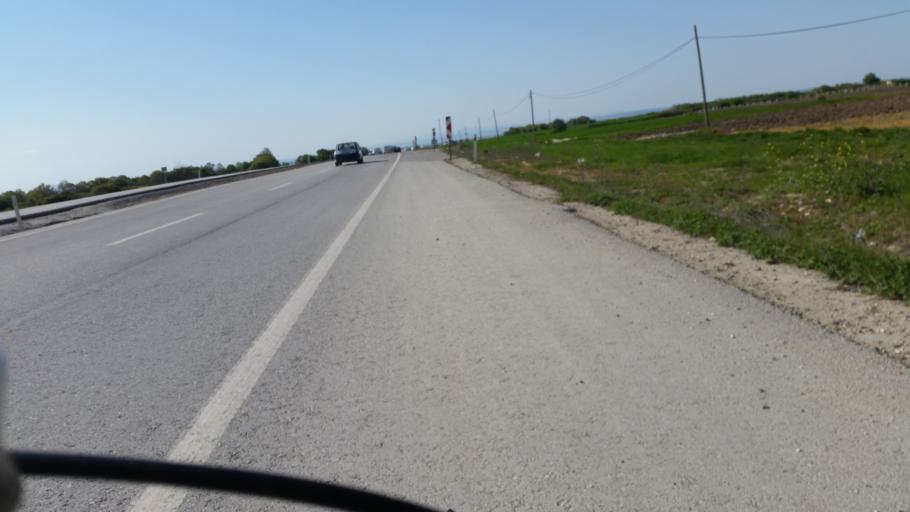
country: TR
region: Tekirdag
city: Cerkezkoey
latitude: 41.3426
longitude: 27.9638
